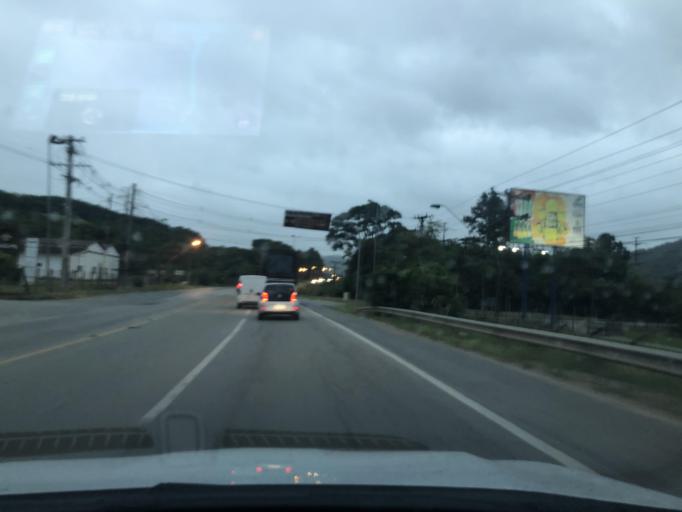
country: BR
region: Santa Catarina
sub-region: Pomerode
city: Pomerode
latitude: -26.7848
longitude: -49.0849
